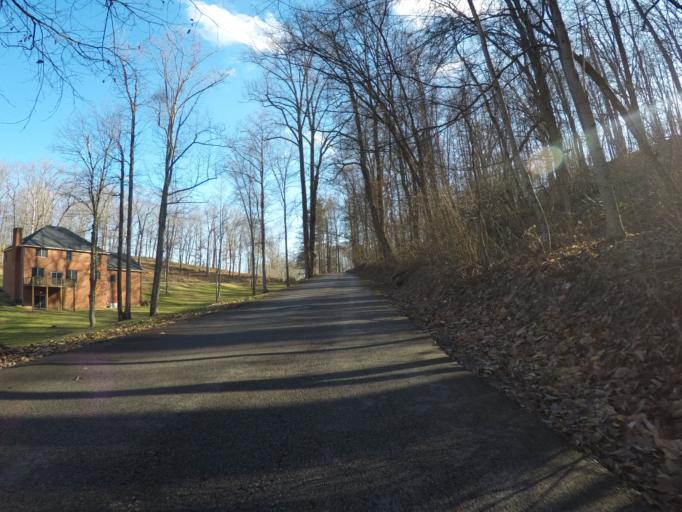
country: US
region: West Virginia
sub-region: Cabell County
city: Pea Ridge
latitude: 38.4017
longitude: -82.3260
